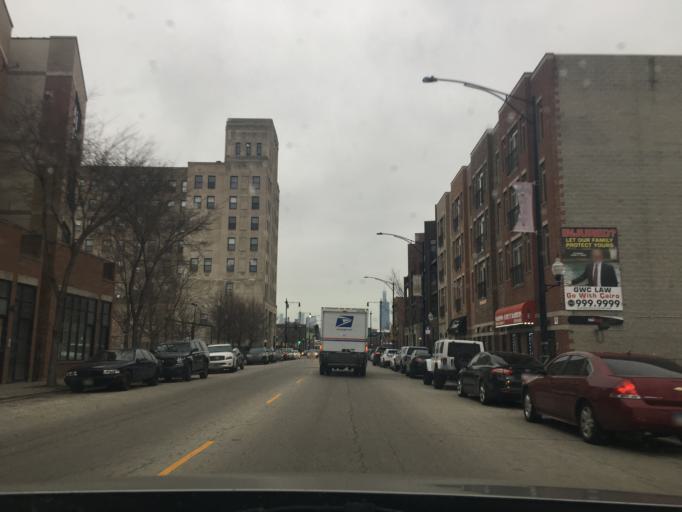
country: US
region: Illinois
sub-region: Cook County
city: Chicago
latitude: 41.8811
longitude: -87.6882
